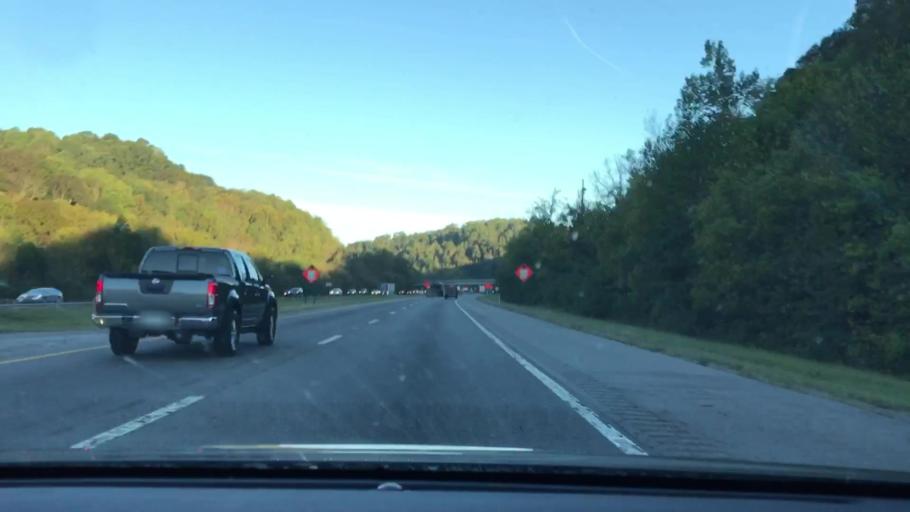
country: US
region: Tennessee
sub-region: Robertson County
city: Ridgetop
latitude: 36.3133
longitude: -86.8303
